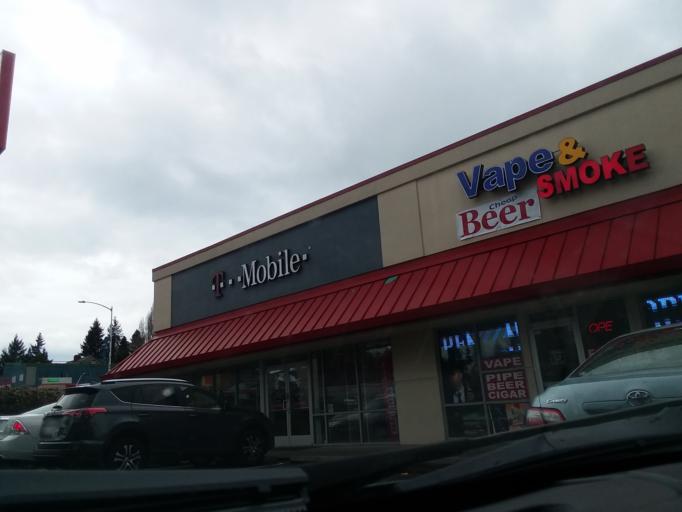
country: US
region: Washington
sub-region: King County
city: Burien
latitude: 47.4762
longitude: -122.3334
